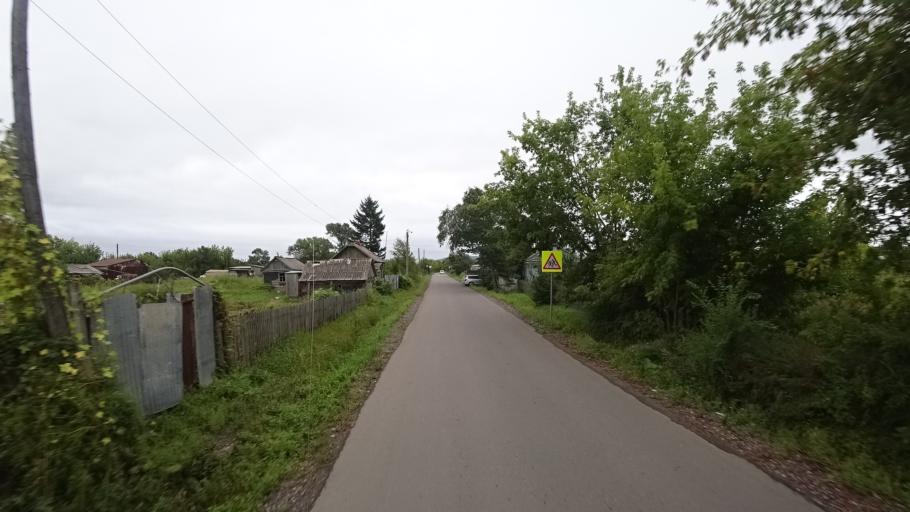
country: RU
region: Primorskiy
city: Chernigovka
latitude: 44.3393
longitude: 132.5368
